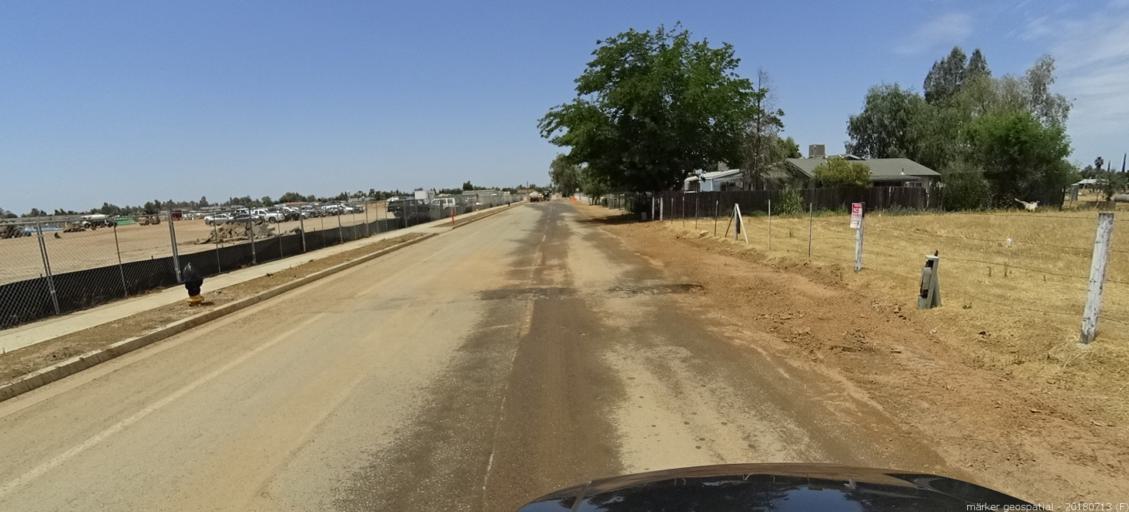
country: US
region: California
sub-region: Madera County
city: Madera Acres
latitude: 36.9927
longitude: -120.0688
